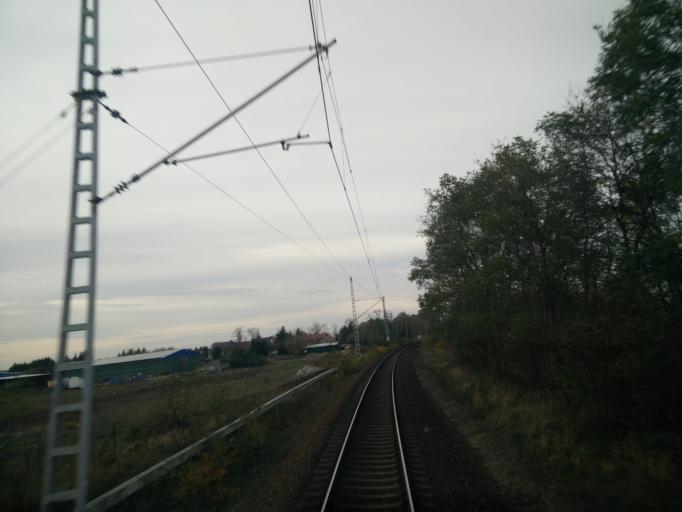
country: DE
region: Brandenburg
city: Vetschau
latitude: 51.7990
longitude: 14.0536
